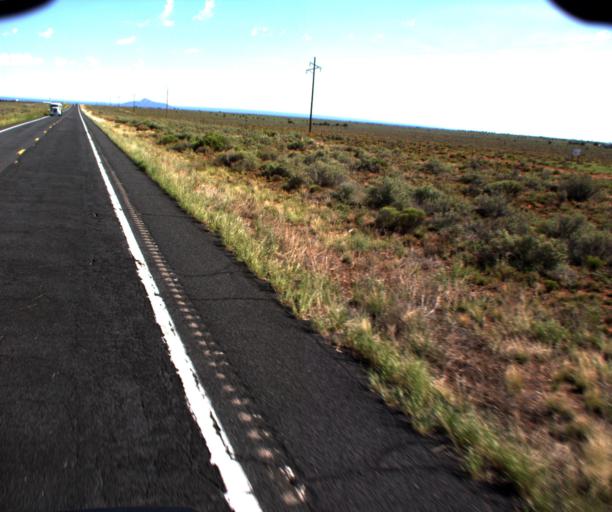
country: US
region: Arizona
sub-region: Coconino County
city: Williams
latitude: 35.6166
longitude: -112.1443
